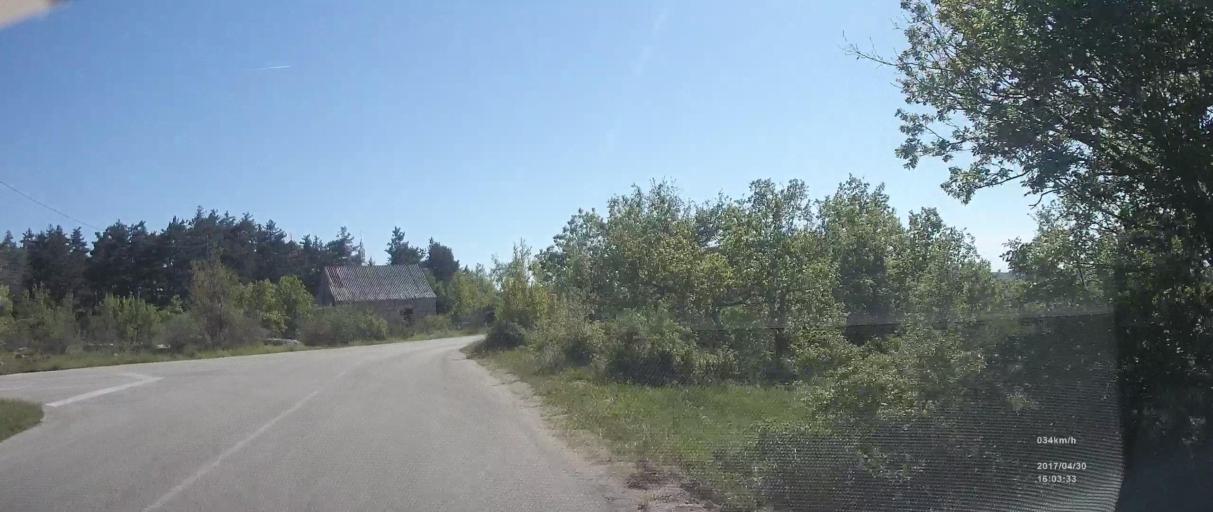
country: HR
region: Splitsko-Dalmatinska
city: Srinjine
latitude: 43.5112
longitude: 16.6062
